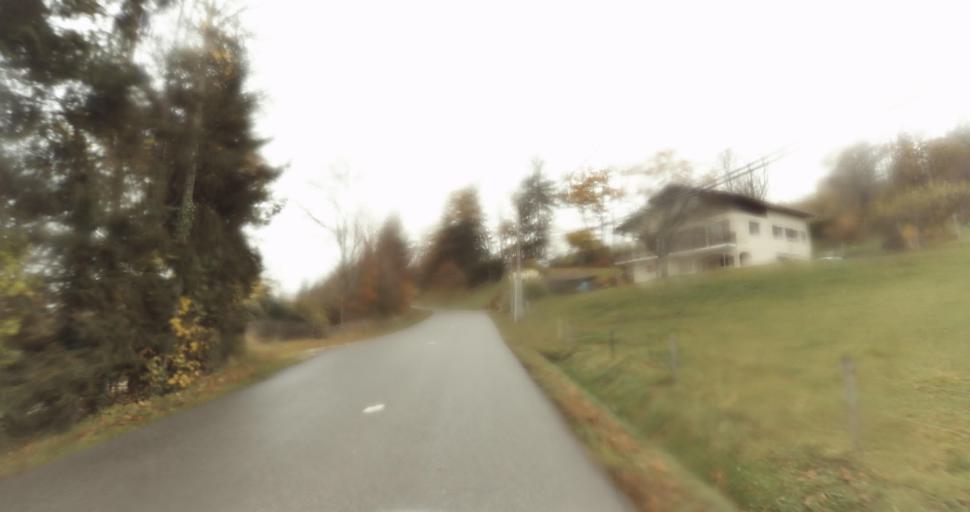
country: FR
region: Rhone-Alpes
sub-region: Departement de la Haute-Savoie
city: Thorens-Glieres
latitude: 46.0029
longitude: 6.2454
